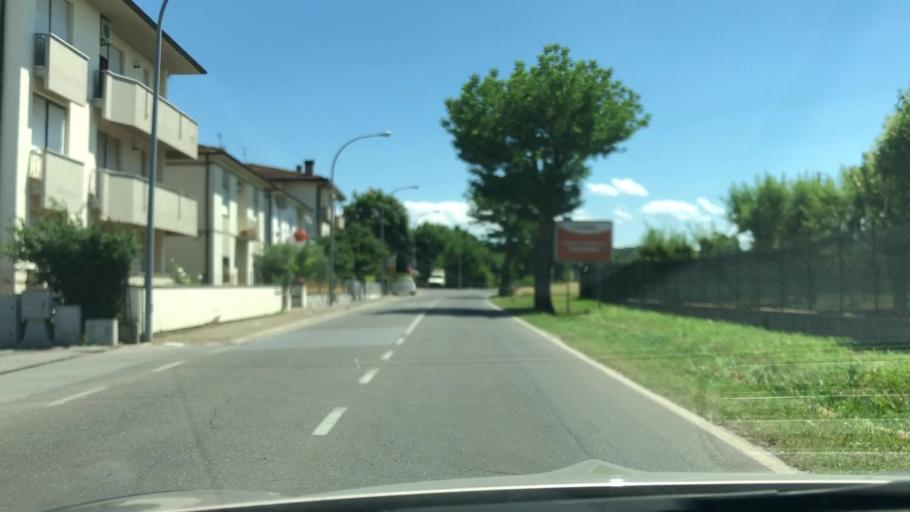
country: IT
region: Tuscany
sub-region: Province of Pisa
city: Ponsacco
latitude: 43.6148
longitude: 10.6412
